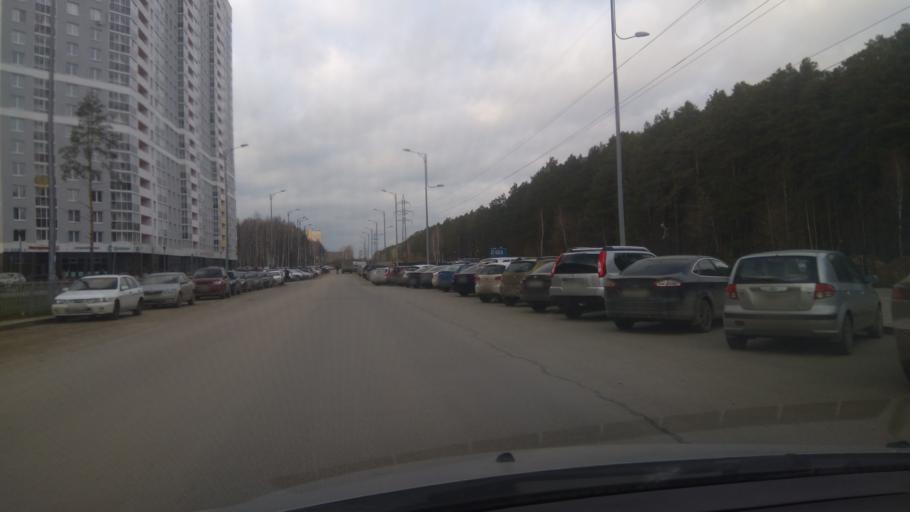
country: RU
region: Sverdlovsk
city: Sovkhoznyy
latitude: 56.7854
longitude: 60.5501
